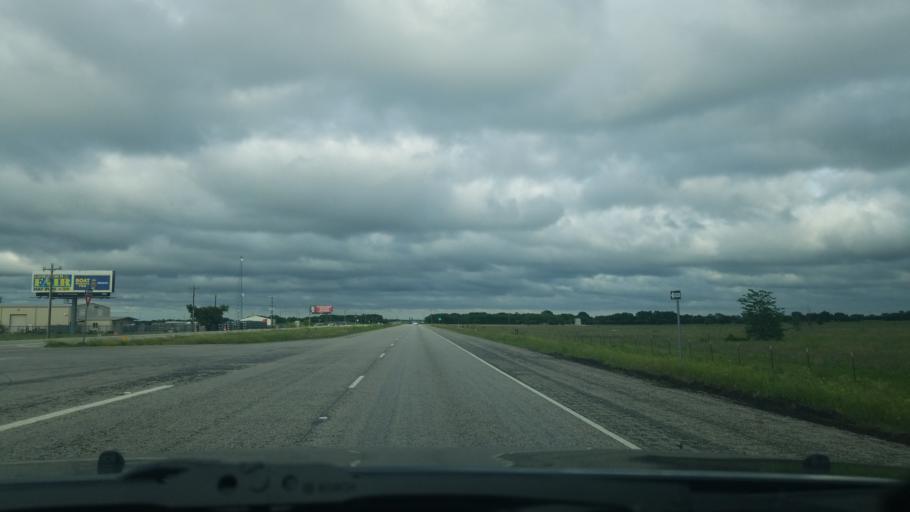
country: US
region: Texas
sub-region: Denton County
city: Ponder
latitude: 33.2388
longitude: -97.3288
